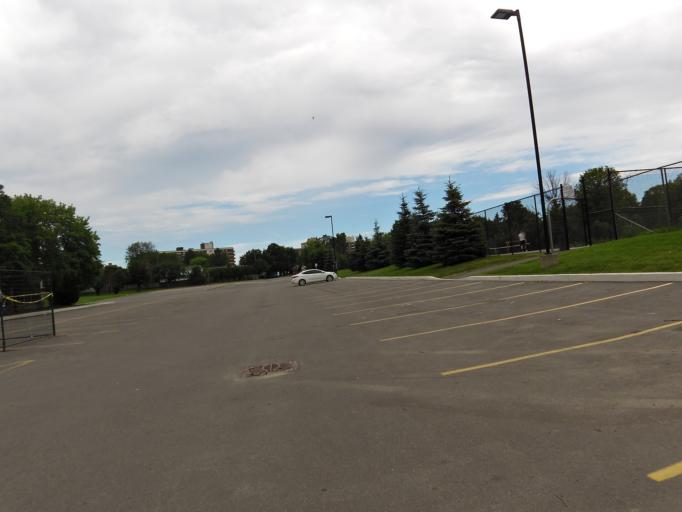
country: CA
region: Ontario
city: Bells Corners
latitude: 45.3624
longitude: -75.7786
